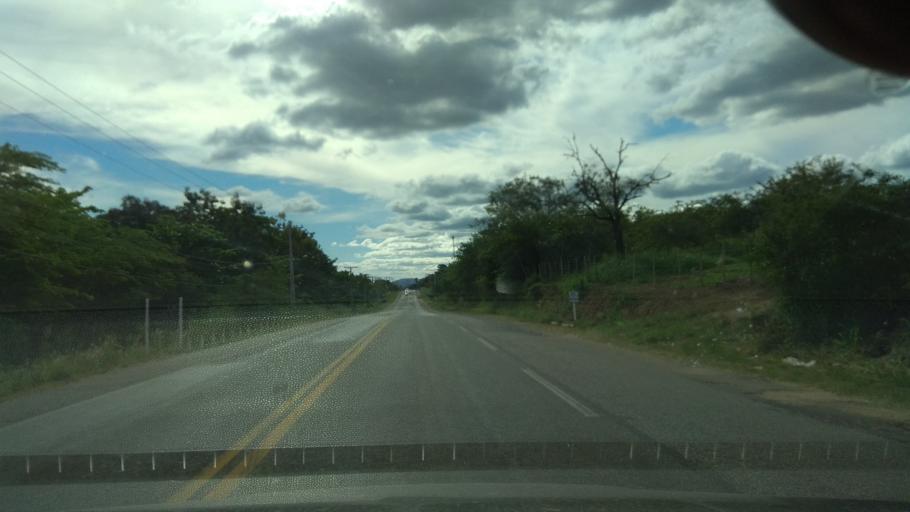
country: BR
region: Bahia
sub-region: Jequie
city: Jequie
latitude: -13.8802
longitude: -40.0346
